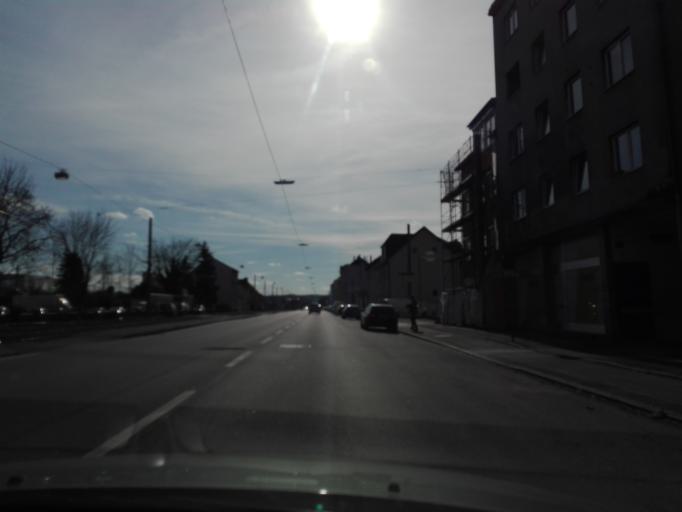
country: AT
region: Upper Austria
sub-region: Linz Stadt
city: Linz
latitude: 48.2676
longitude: 14.3167
